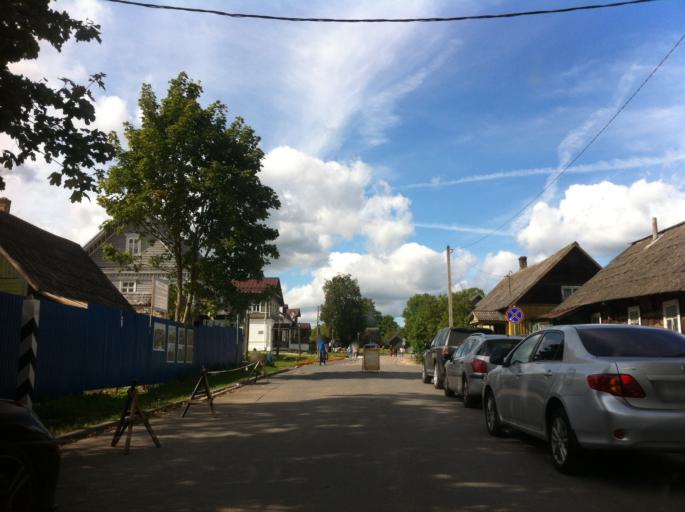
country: RU
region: Pskov
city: Izborsk
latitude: 57.7080
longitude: 27.8598
